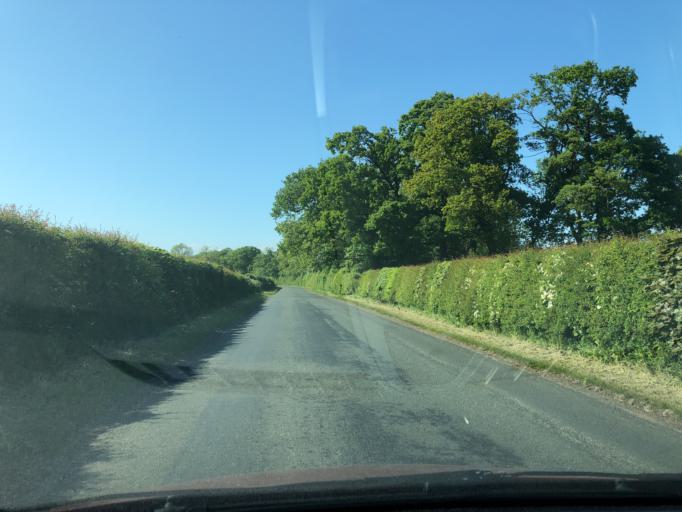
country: GB
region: England
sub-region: North Yorkshire
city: Northallerton
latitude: 54.3153
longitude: -1.3742
